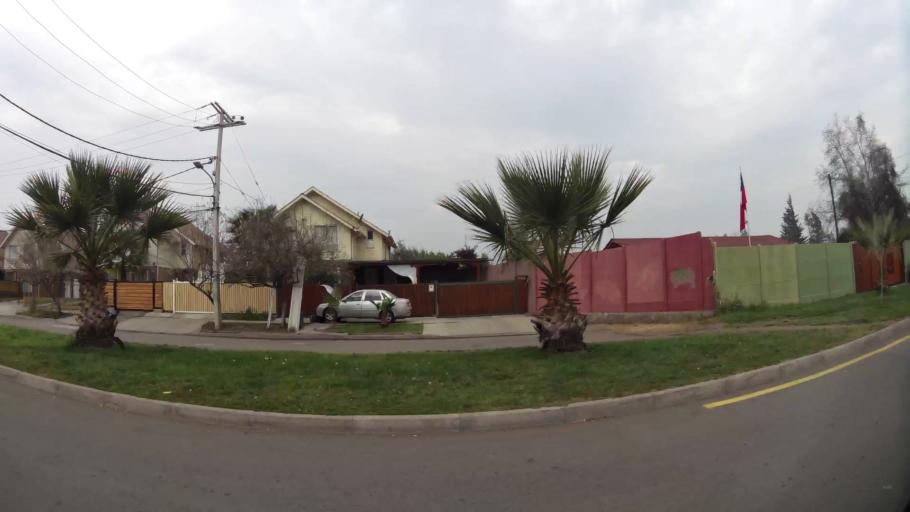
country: CL
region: Santiago Metropolitan
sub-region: Provincia de Chacabuco
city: Chicureo Abajo
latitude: -33.2027
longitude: -70.6820
